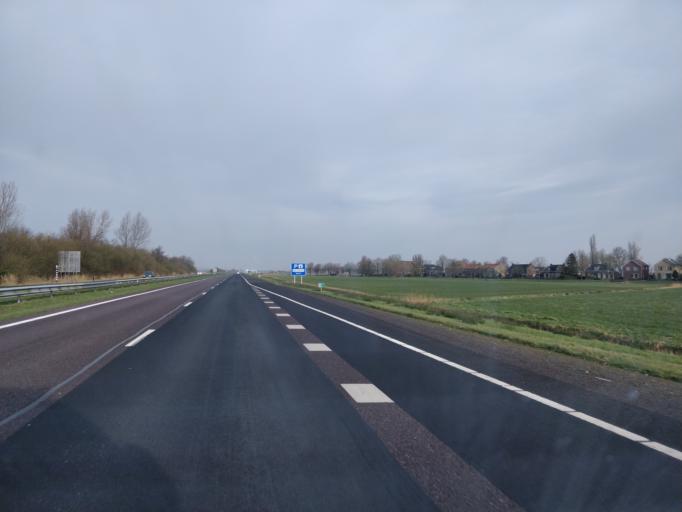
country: NL
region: Friesland
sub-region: Gemeente Boarnsterhim
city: Reduzum
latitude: 53.1184
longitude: 5.8094
